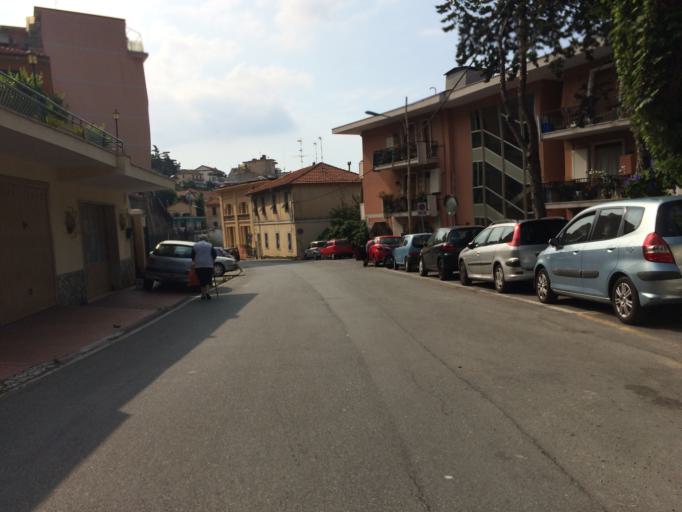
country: IT
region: Liguria
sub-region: Provincia di Imperia
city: San Remo
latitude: 43.8258
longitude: 7.7737
